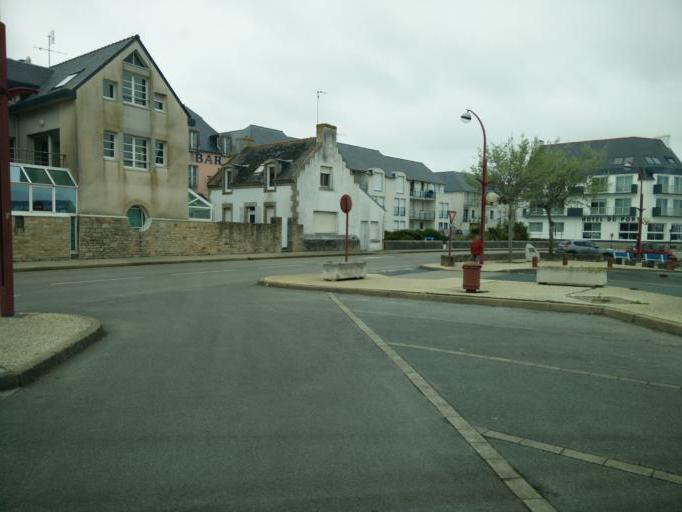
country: FR
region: Brittany
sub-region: Departement du Finistere
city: Plobannalec-Lesconil
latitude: 47.7969
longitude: -4.2153
